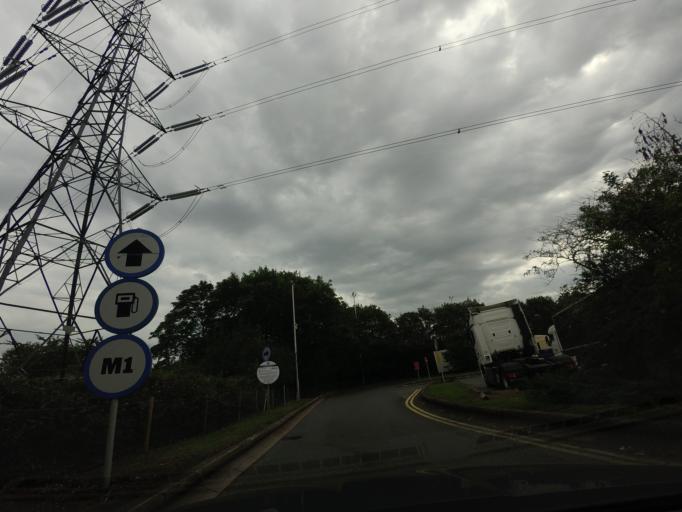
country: GB
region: England
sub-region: Central Bedfordshire
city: Harlington
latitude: 51.9489
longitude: -0.5004
